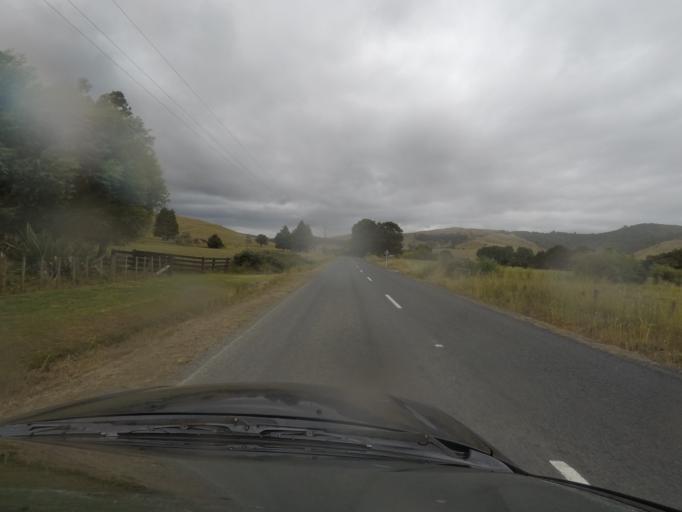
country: NZ
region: Auckland
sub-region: Auckland
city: Warkworth
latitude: -36.2777
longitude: 174.6765
